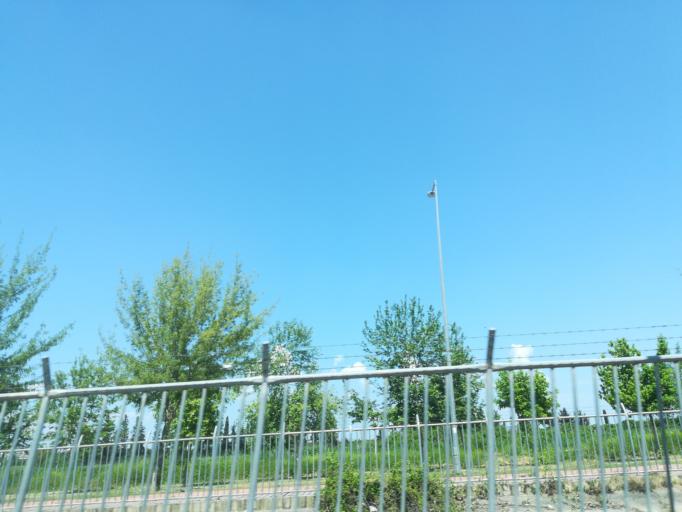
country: TR
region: Adana
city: Yuregir
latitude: 37.0188
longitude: 35.3737
